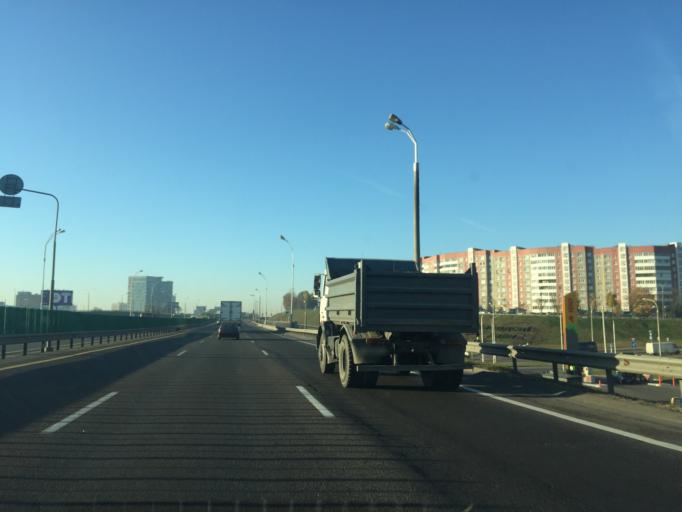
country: BY
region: Minsk
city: Vyaliki Trastsyanets
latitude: 53.8701
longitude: 27.6914
